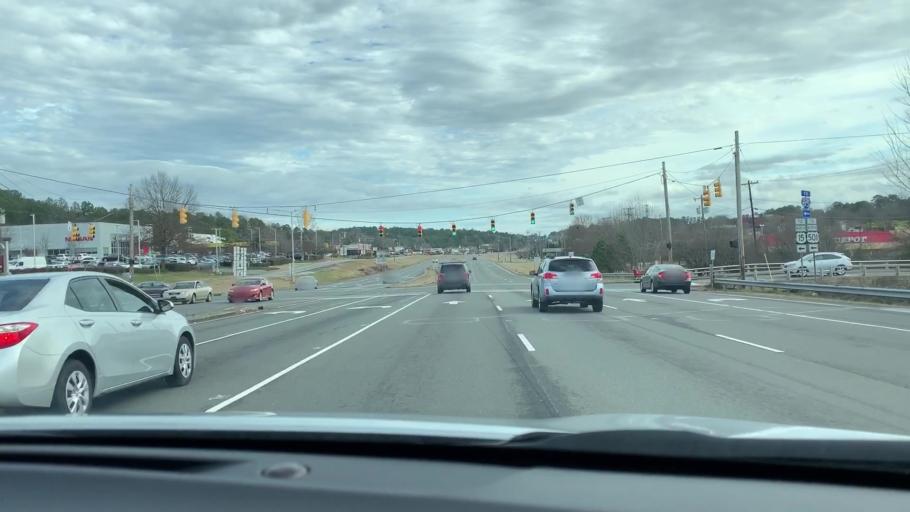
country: US
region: North Carolina
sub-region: Durham County
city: Durham
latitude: 35.9694
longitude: -78.9583
